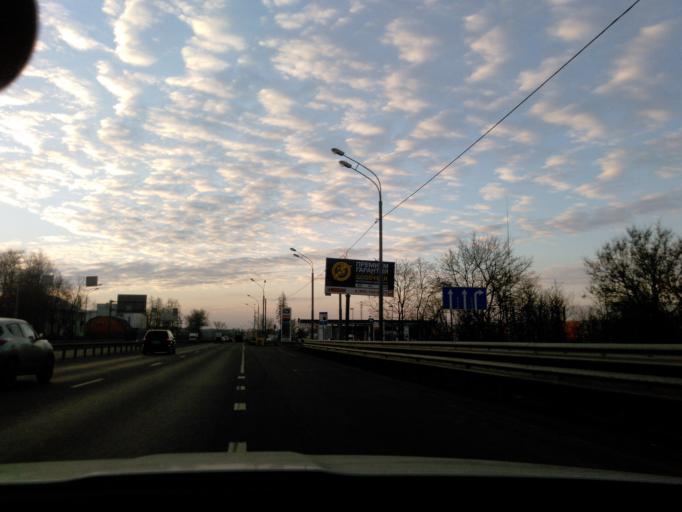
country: RU
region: Moskovskaya
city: Skhodnya
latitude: 55.9771
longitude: 37.3021
